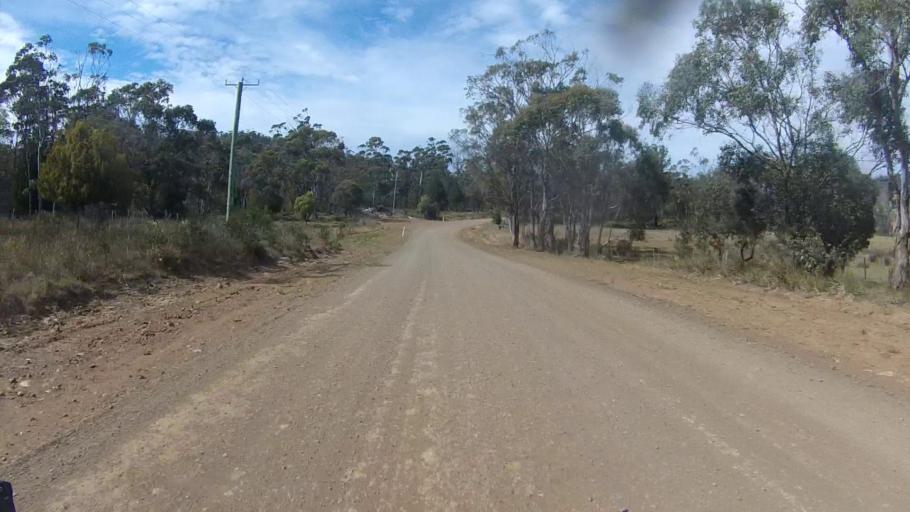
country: AU
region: Tasmania
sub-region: Sorell
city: Sorell
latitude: -42.6474
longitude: 147.8995
